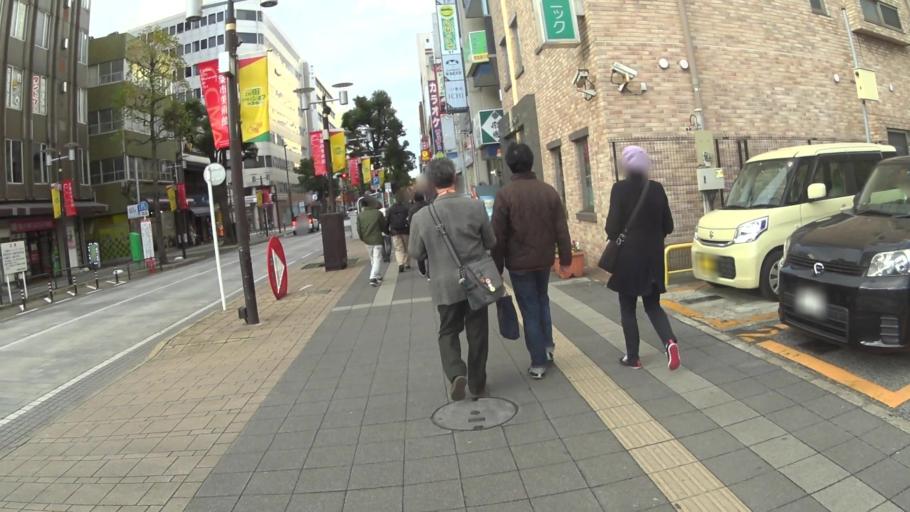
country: JP
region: Chiba
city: Chiba
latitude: 35.6079
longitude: 140.1220
